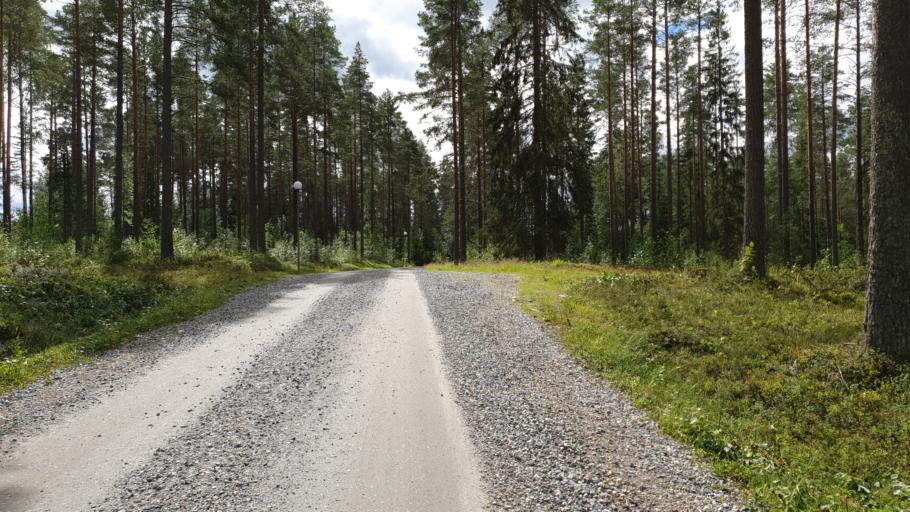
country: FI
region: Kainuu
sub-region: Kehys-Kainuu
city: Kuhmo
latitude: 64.3913
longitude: 29.8283
